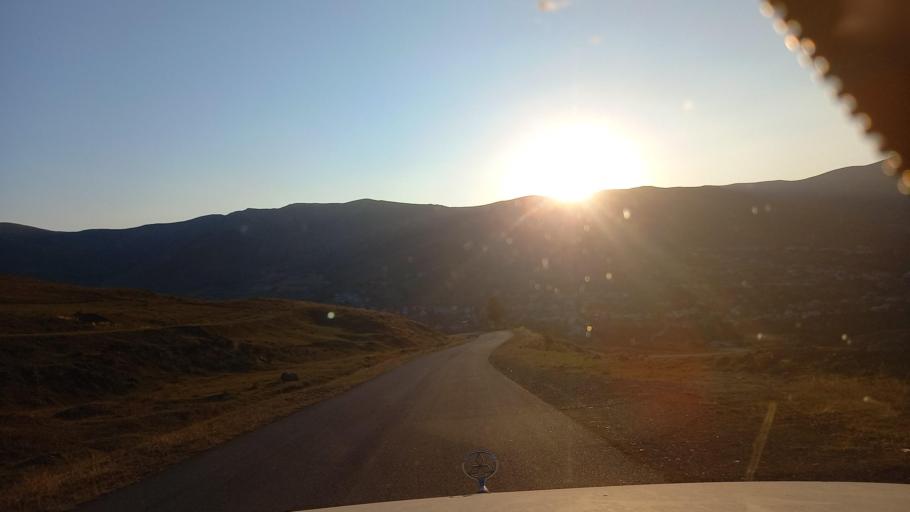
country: AZ
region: Gadabay Rayon
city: Ariqdam
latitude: 40.6835
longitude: 45.7755
